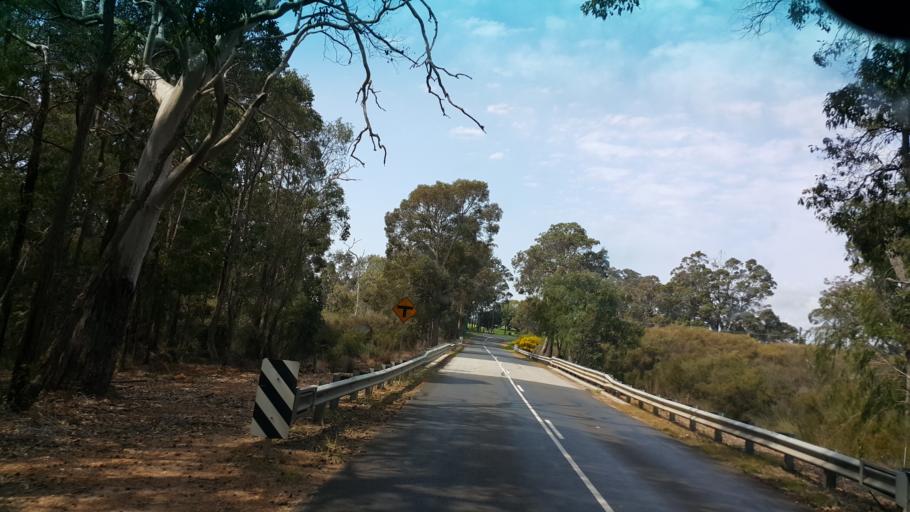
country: AU
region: Western Australia
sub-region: Busselton
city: Vasse
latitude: -33.7483
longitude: 115.1891
